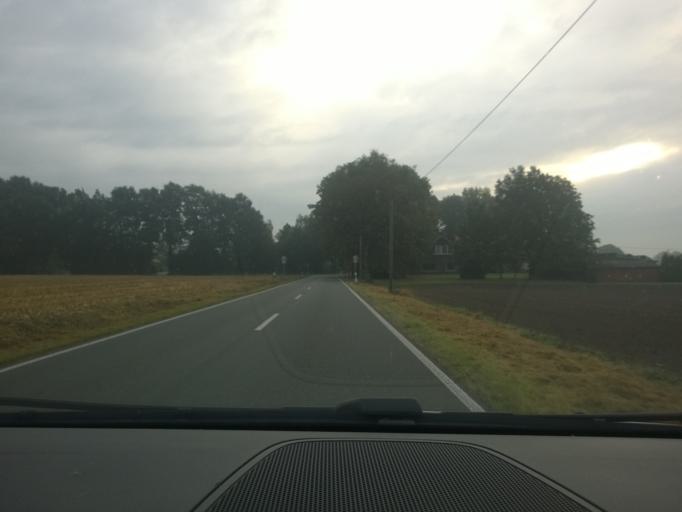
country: DE
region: North Rhine-Westphalia
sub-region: Regierungsbezirk Munster
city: Sudlohn
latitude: 51.9481
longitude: 6.8913
